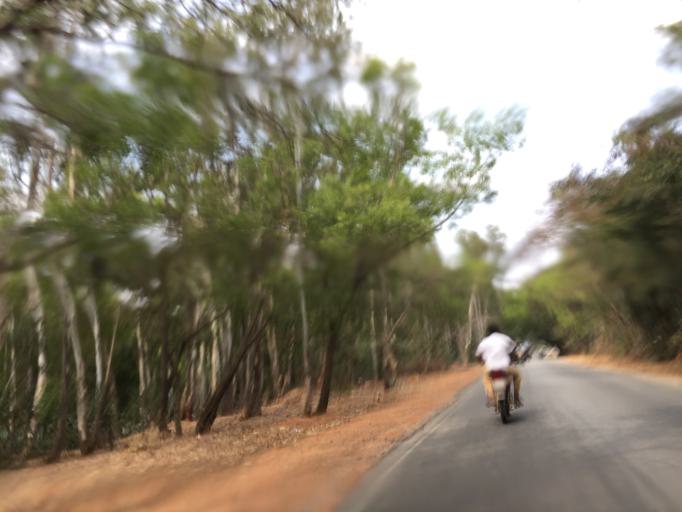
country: IN
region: Karnataka
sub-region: Chikkaballapur
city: Chik Ballapur
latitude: 13.3999
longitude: 77.7066
